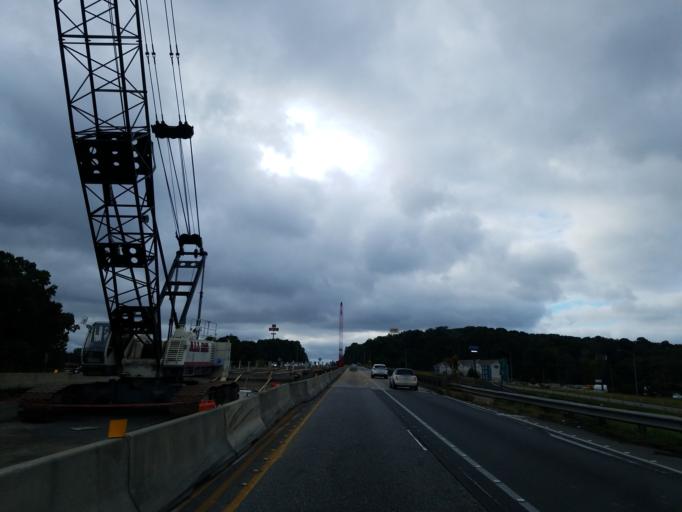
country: US
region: Alabama
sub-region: Tuscaloosa County
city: Holt
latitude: 33.1741
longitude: -87.4734
